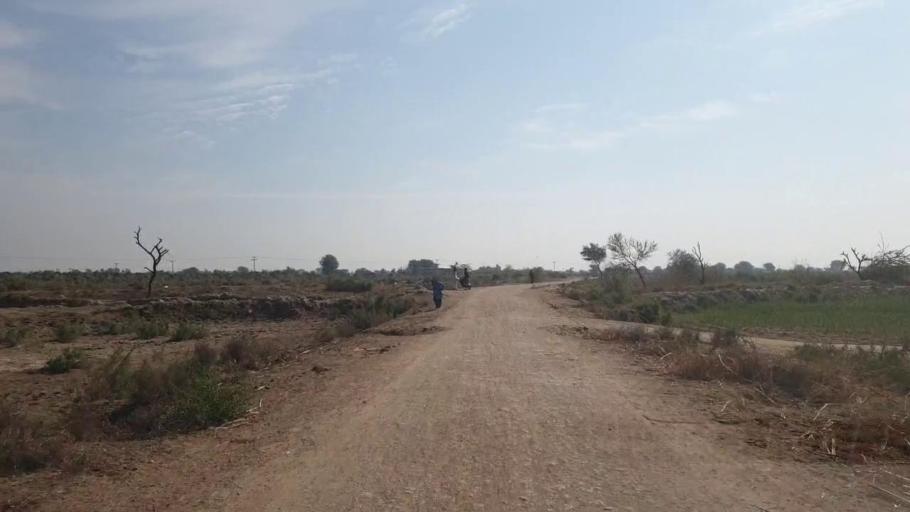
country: PK
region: Sindh
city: Mirwah Gorchani
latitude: 25.3670
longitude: 69.1893
